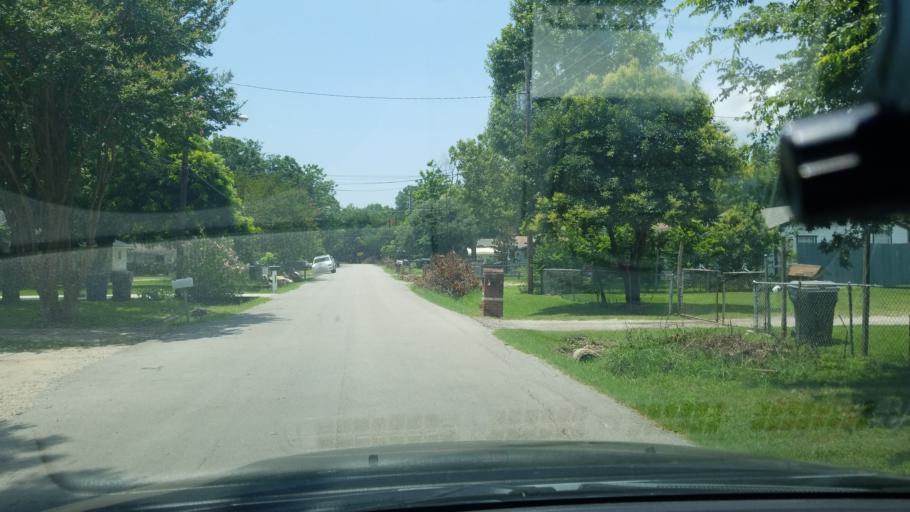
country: US
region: Texas
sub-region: Dallas County
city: Balch Springs
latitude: 32.7283
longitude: -96.6689
